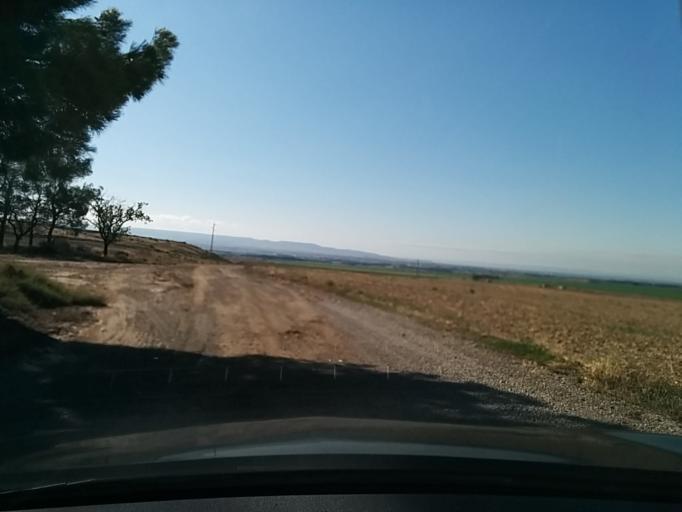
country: ES
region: Aragon
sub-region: Provincia de Zaragoza
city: Tauste
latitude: 42.0126
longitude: -1.3036
